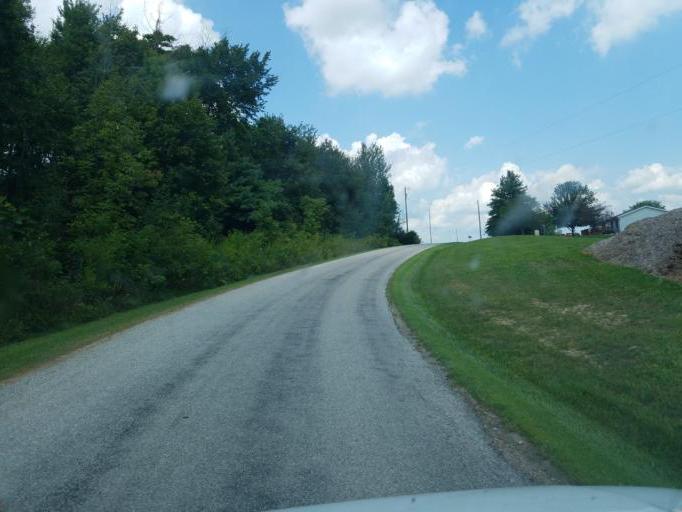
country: US
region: Ohio
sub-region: Knox County
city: Centerburg
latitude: 40.3921
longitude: -82.6778
